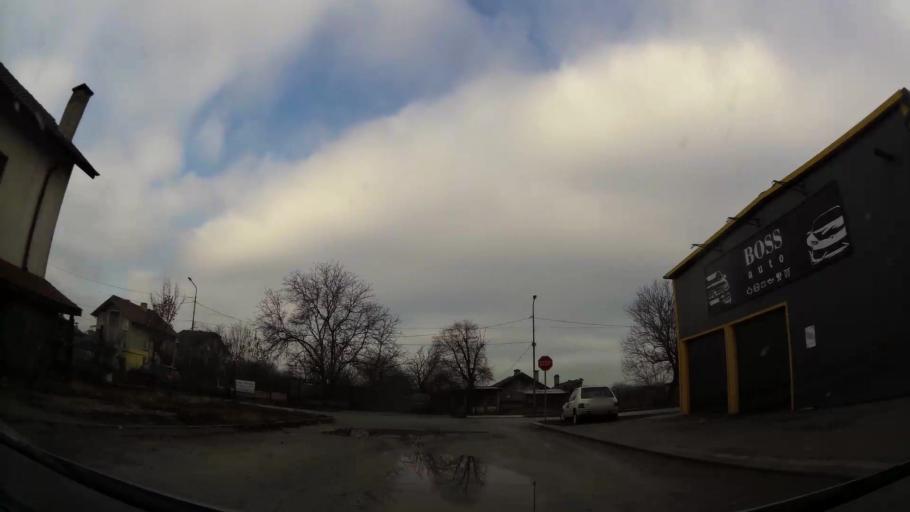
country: BG
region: Sofia-Capital
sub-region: Stolichna Obshtina
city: Sofia
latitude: 42.7482
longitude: 23.3511
